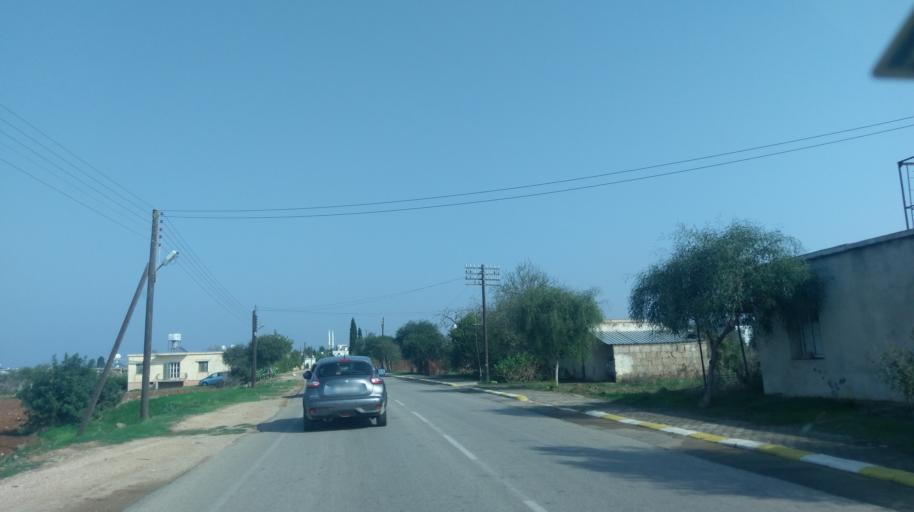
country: CY
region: Ammochostos
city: Leonarisso
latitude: 35.5276
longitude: 34.1815
